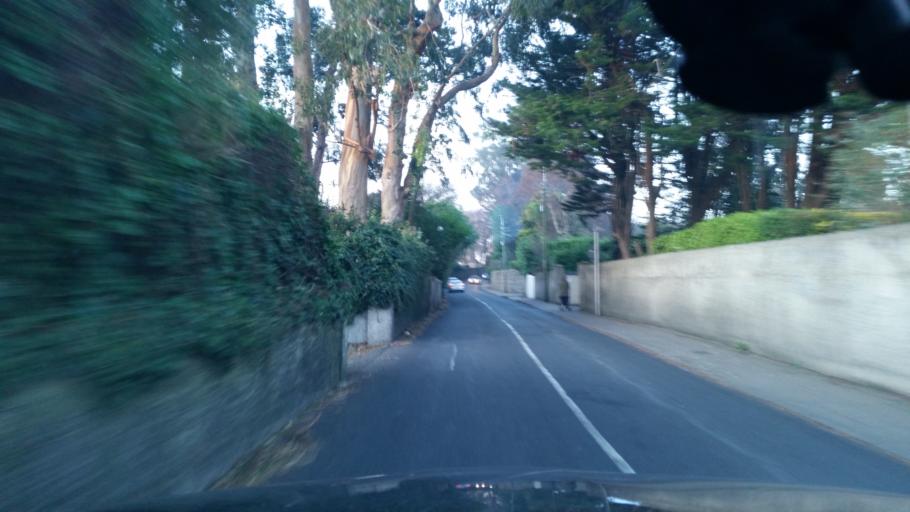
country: IE
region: Leinster
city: Loughlinstown
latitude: 53.2490
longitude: -6.1197
